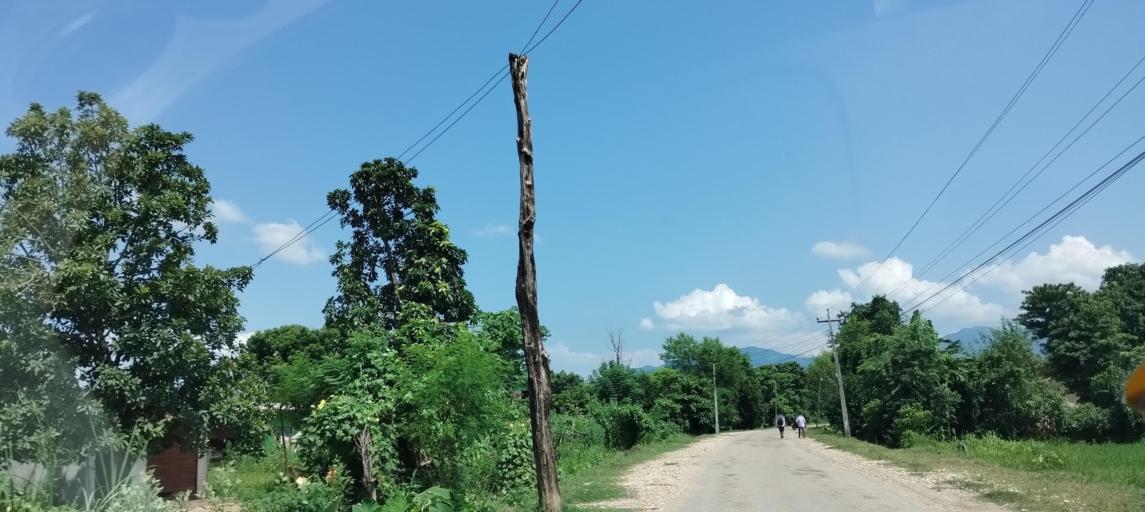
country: NP
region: Far Western
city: Tikapur
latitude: 28.5030
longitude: 81.3021
